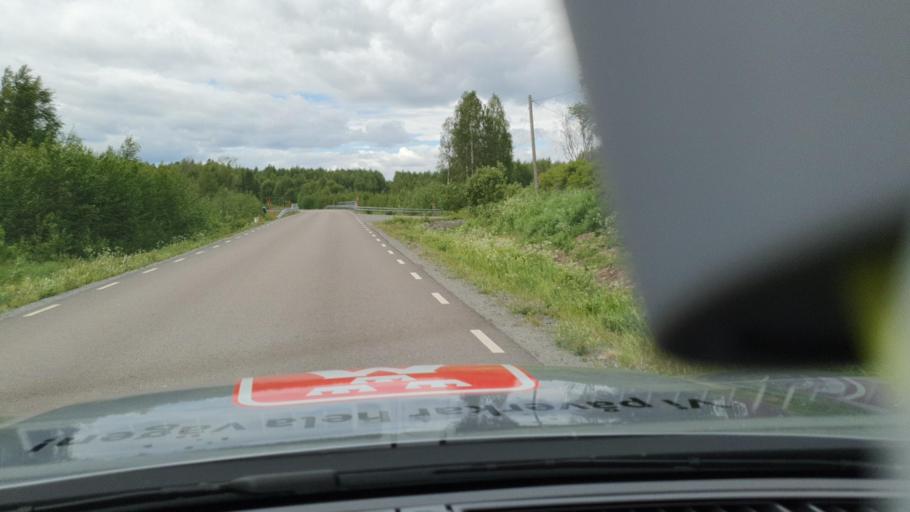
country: SE
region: Norrbotten
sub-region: Lulea Kommun
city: Sodra Sunderbyn
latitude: 65.8434
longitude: 21.9315
